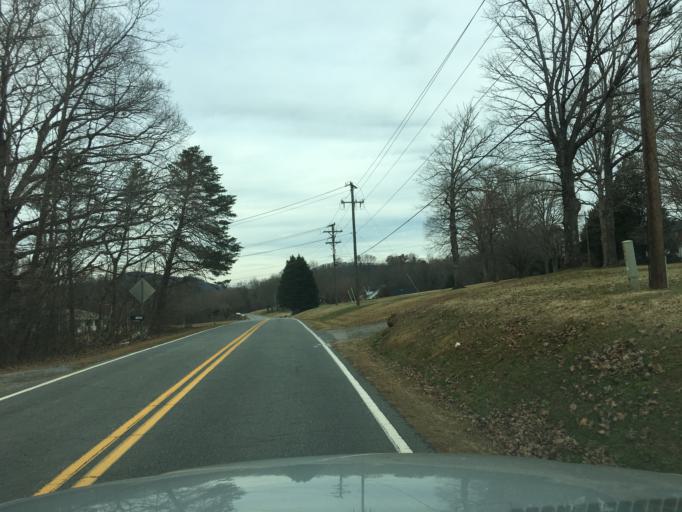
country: US
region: North Carolina
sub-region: McDowell County
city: West Marion
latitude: 35.6187
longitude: -81.9814
